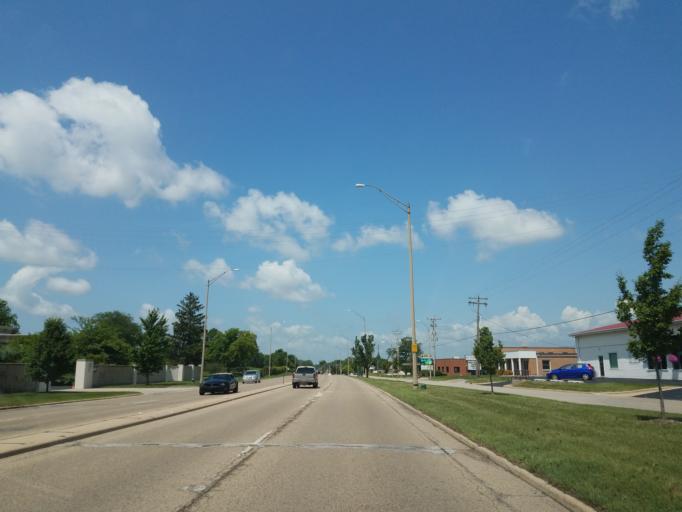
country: US
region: Illinois
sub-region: McLean County
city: Bloomington
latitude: 40.4884
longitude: -88.9628
